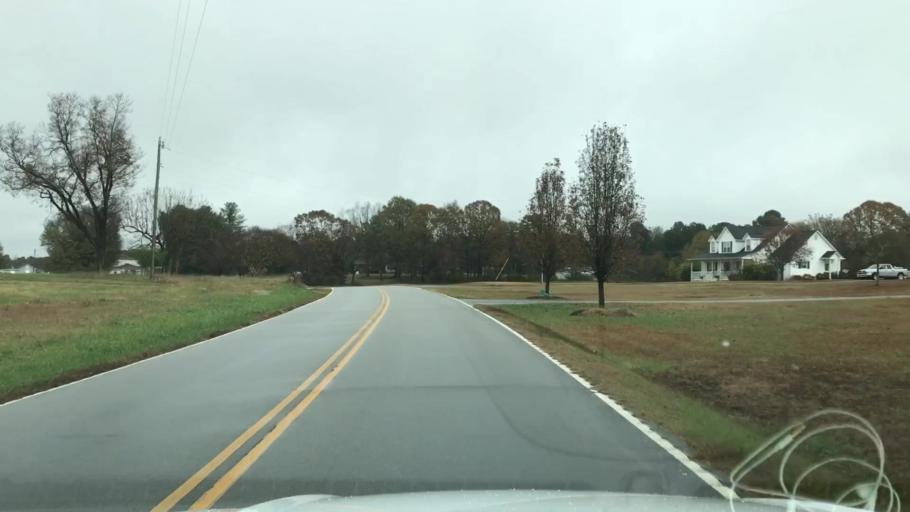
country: US
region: South Carolina
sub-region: Spartanburg County
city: Roebuck
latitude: 34.7914
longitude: -81.9151
